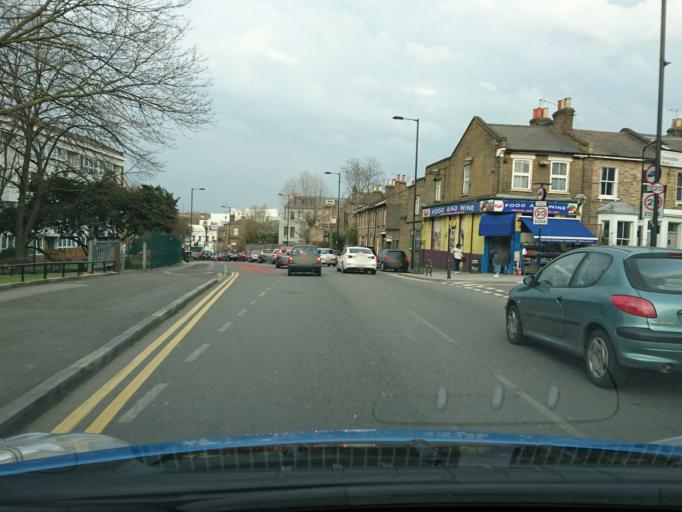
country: GB
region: England
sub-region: Greater London
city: Hackney
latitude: 51.5443
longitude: -0.0373
